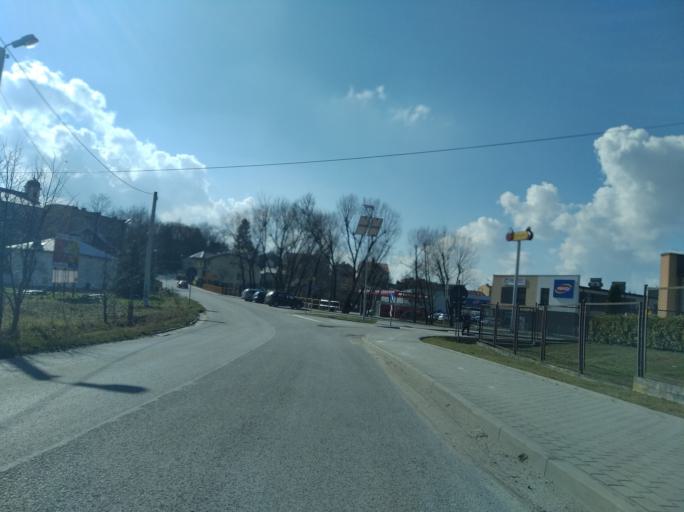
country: PL
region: Subcarpathian Voivodeship
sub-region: Powiat debicki
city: Brzostek
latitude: 49.8813
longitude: 21.4138
